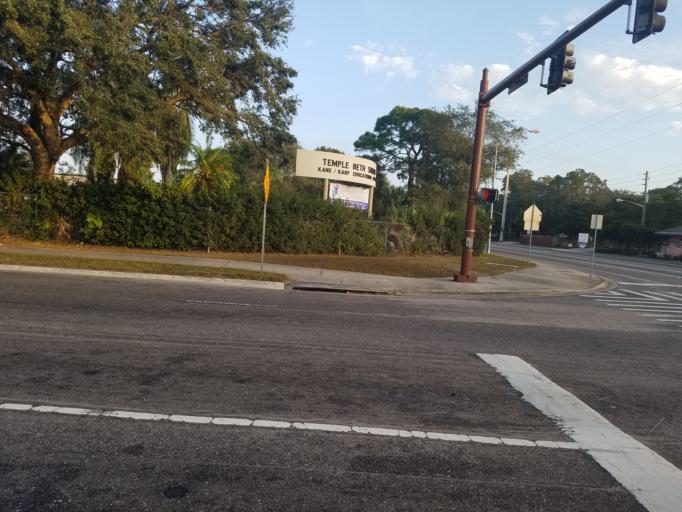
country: US
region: Florida
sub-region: Sarasota County
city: Southgate
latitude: 27.3229
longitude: -82.5146
